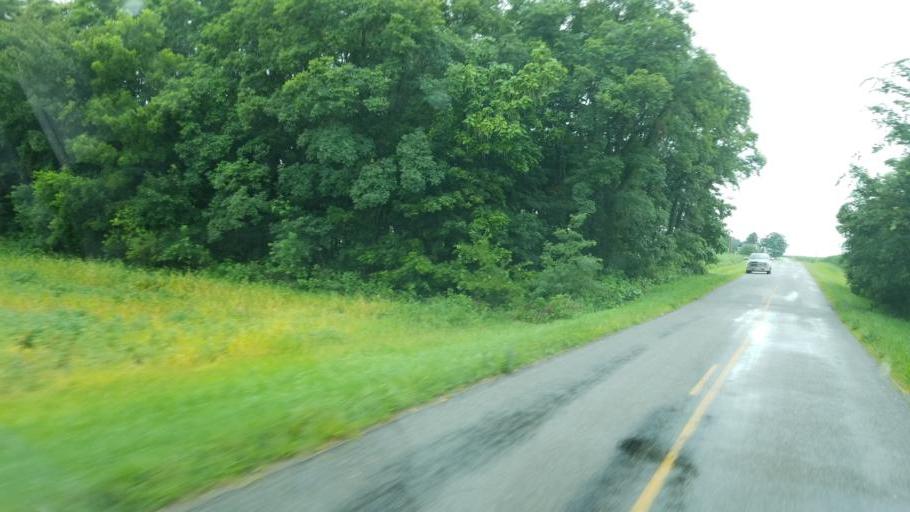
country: US
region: Ohio
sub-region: Hardin County
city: Kenton
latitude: 40.5092
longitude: -83.4910
